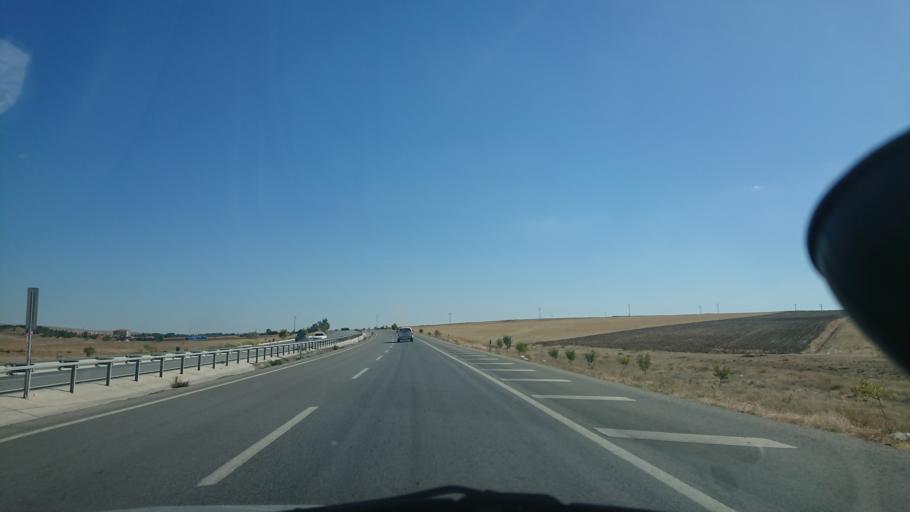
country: TR
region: Eskisehir
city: Mahmudiye
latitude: 39.5006
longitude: 30.9680
